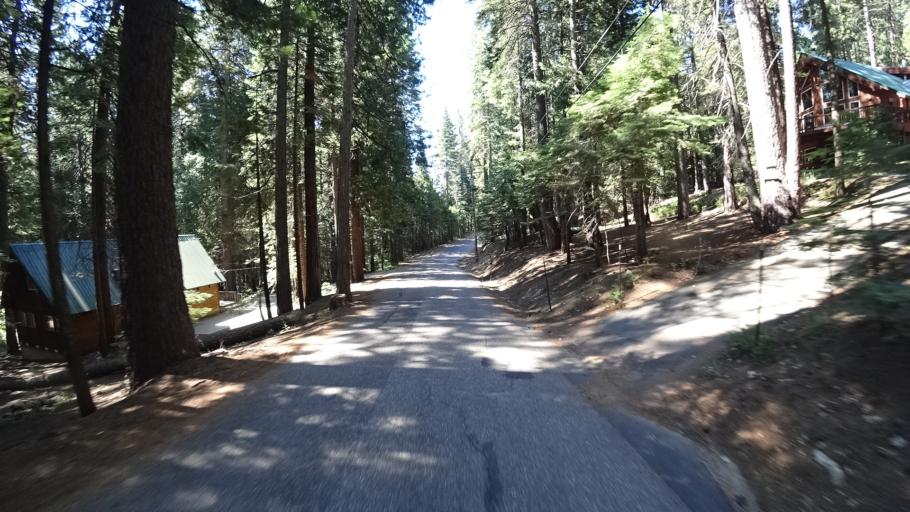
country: US
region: California
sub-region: Calaveras County
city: Arnold
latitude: 38.2973
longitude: -120.2754
